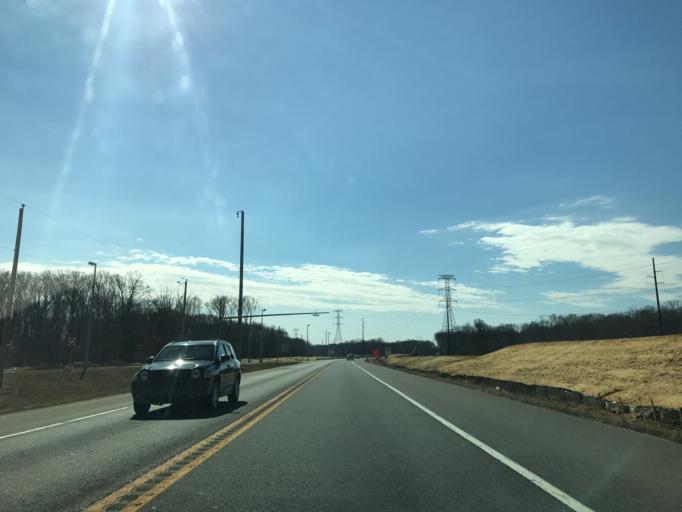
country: US
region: Delaware
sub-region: New Castle County
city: Middletown
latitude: 39.4197
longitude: -75.7641
